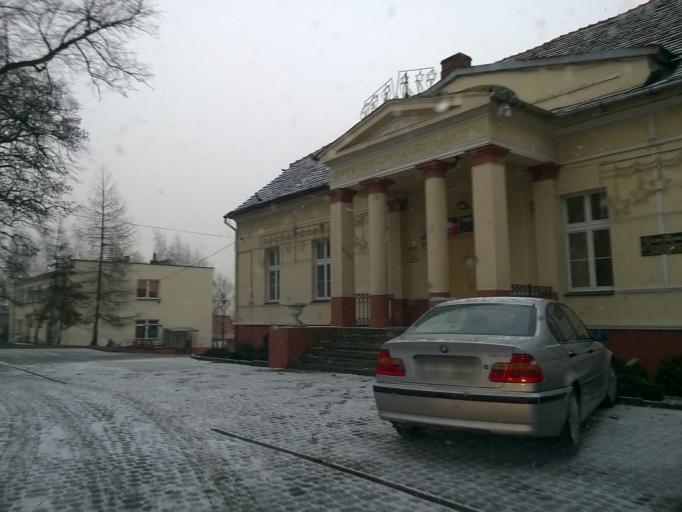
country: PL
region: Kujawsko-Pomorskie
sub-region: Powiat nakielski
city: Kcynia
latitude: 52.9896
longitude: 17.4876
